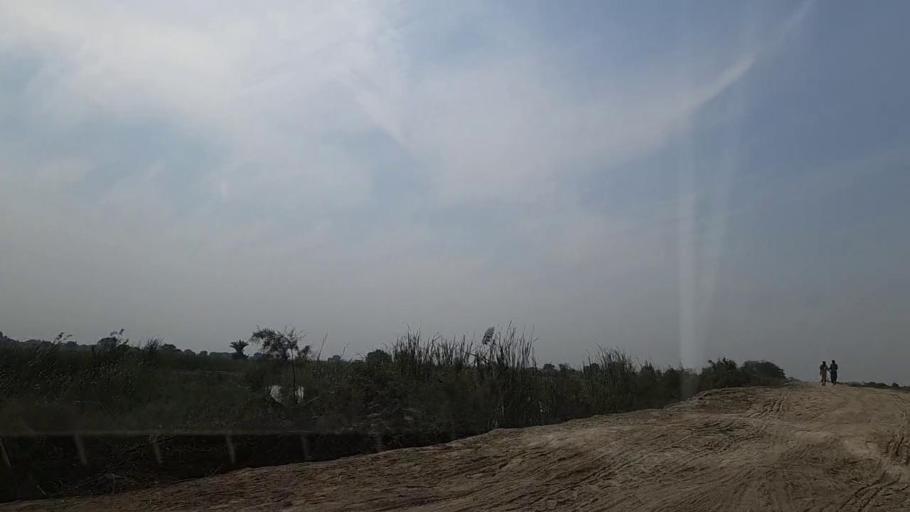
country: PK
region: Sindh
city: Mirpur Batoro
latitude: 24.6616
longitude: 68.2506
